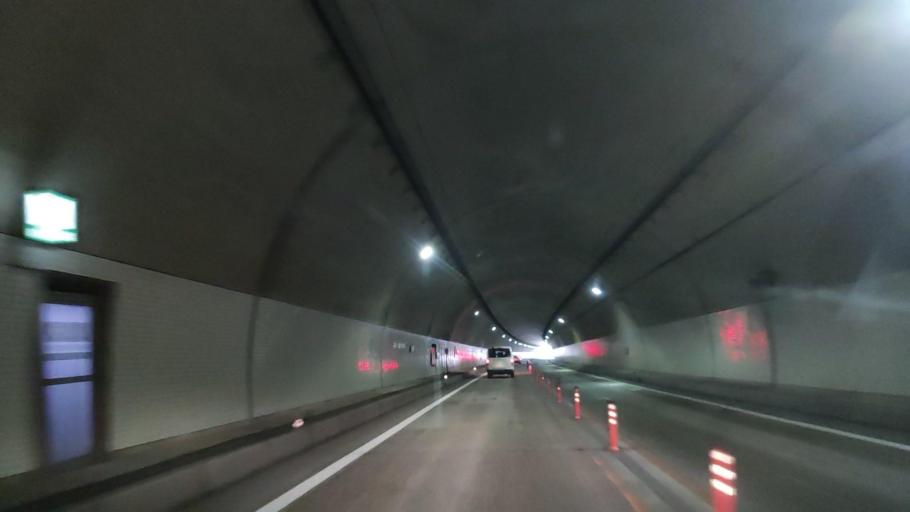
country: JP
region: Akita
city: Odate
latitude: 40.3309
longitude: 140.6091
